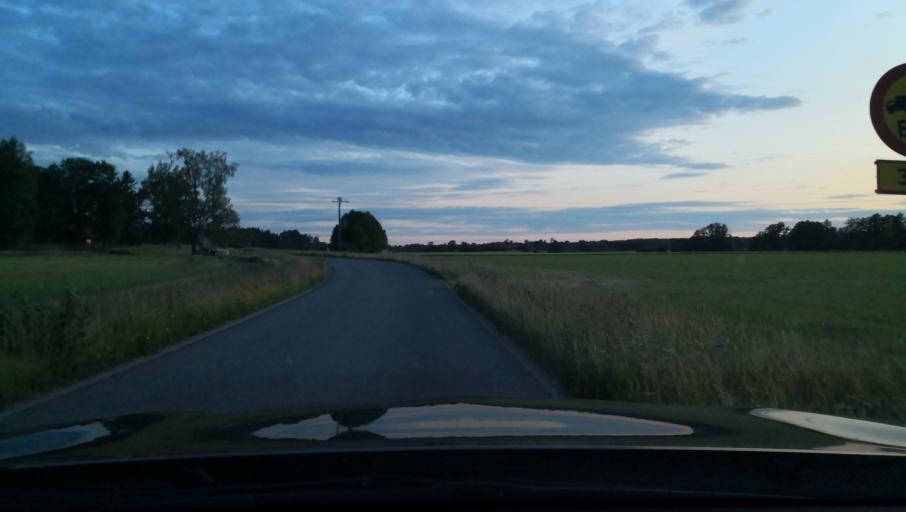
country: SE
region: Uppsala
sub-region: Osthammars Kommun
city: Bjorklinge
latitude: 60.0396
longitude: 17.5023
